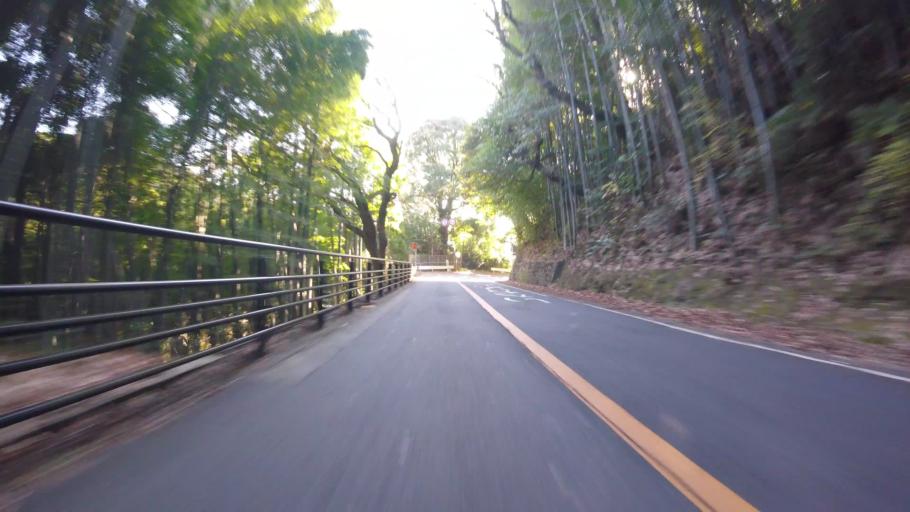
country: JP
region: Shizuoka
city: Atami
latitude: 35.1032
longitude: 139.0646
